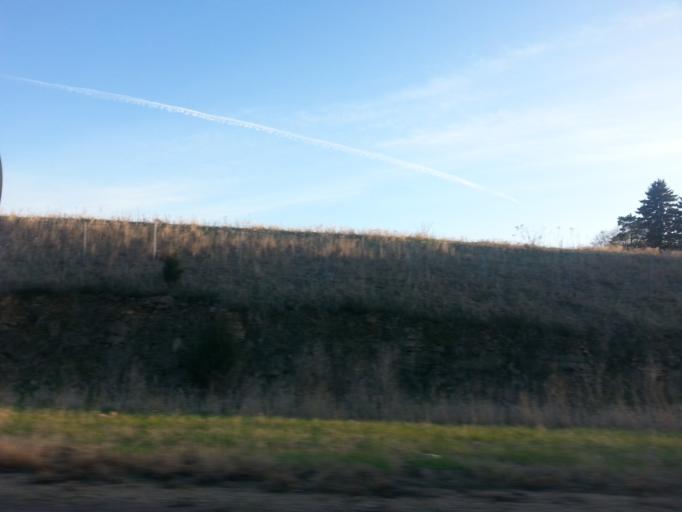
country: US
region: Minnesota
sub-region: Dakota County
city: Hastings
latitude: 44.7620
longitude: -92.8493
